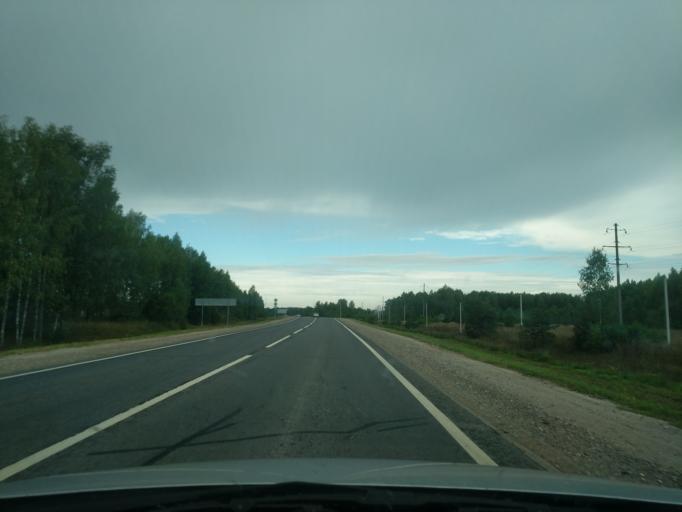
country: RU
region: Kostroma
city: Ostrovskoye
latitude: 57.8084
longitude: 42.2888
